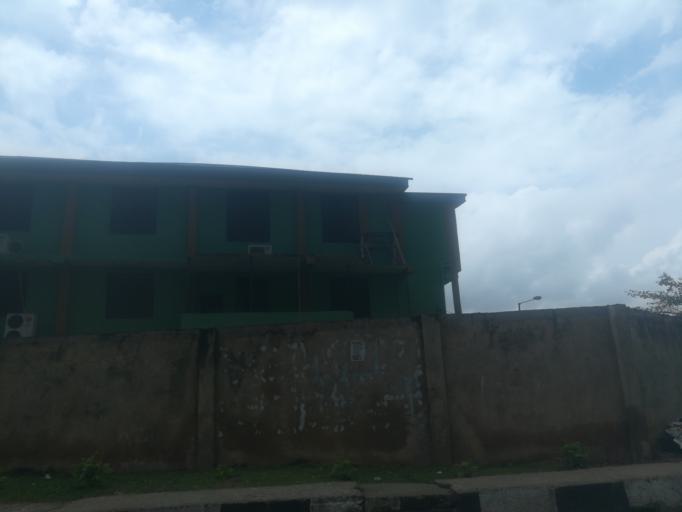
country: NG
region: Lagos
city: Ojota
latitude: 6.5900
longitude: 3.3866
